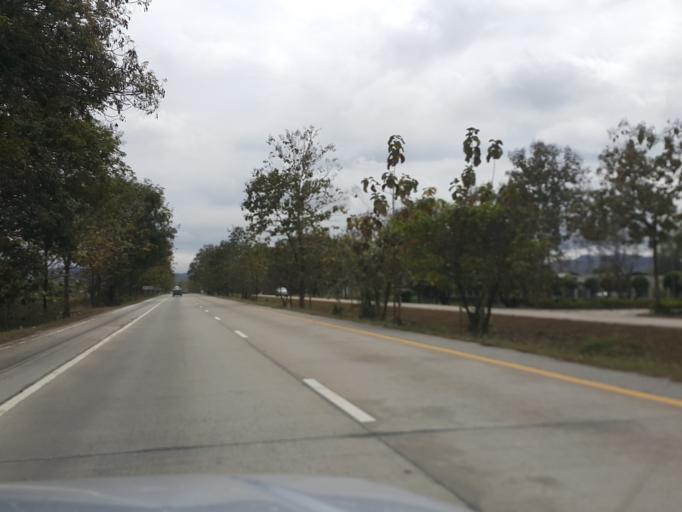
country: TH
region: Lamphun
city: Lamphun
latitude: 18.5328
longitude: 99.0772
